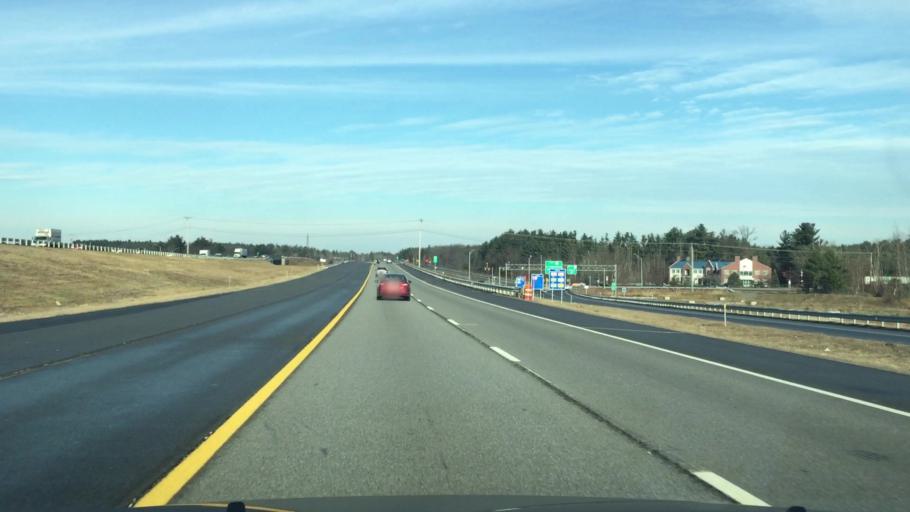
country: US
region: New Hampshire
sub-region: Rockingham County
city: Londonderry
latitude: 42.9136
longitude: -71.3692
